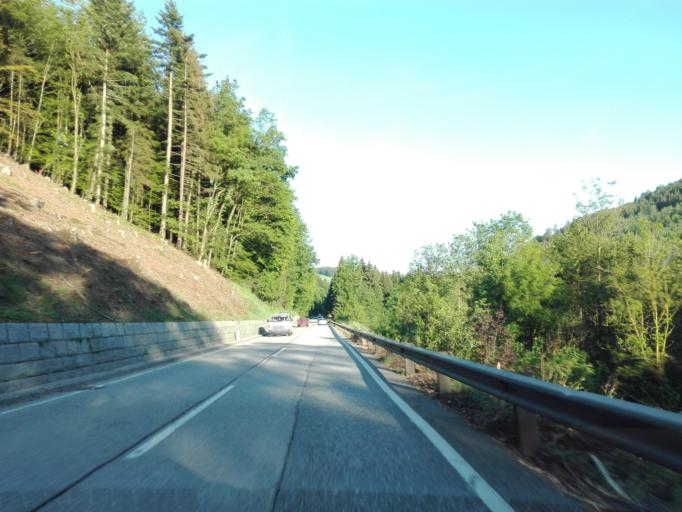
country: AT
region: Upper Austria
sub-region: Politischer Bezirk Rohrbach
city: Kleinzell im Muehlkreis
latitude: 48.3926
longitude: 13.9279
